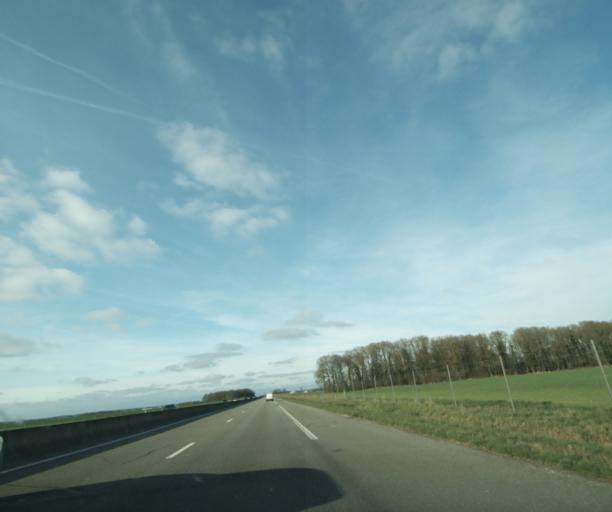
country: FR
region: Ile-de-France
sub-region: Departement des Yvelines
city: Rambouillet
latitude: 48.6019
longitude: 1.8318
